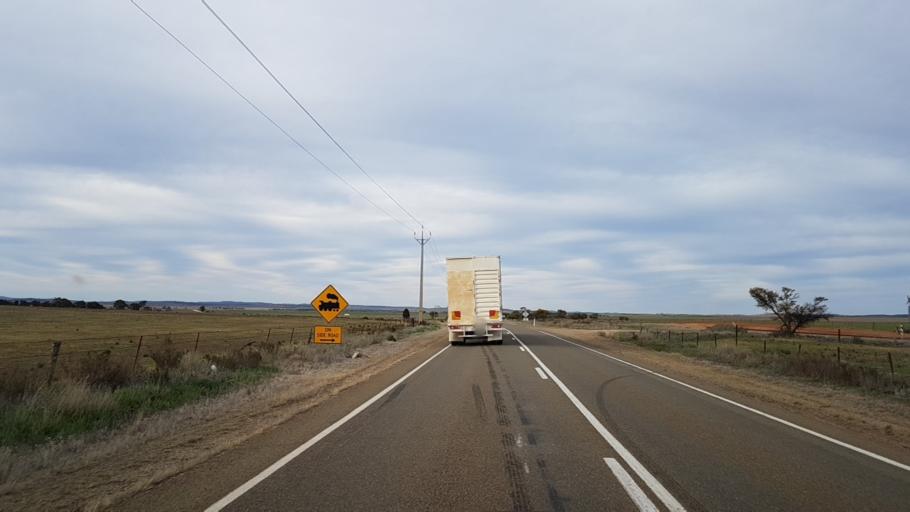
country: AU
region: South Australia
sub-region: Peterborough
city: Peterborough
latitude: -33.0163
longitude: 138.7578
